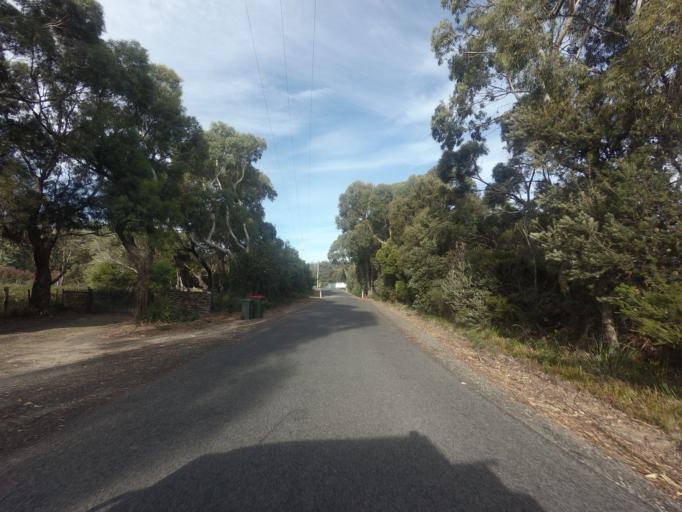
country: AU
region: Tasmania
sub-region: Sorell
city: Sorell
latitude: -42.9702
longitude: 147.8331
